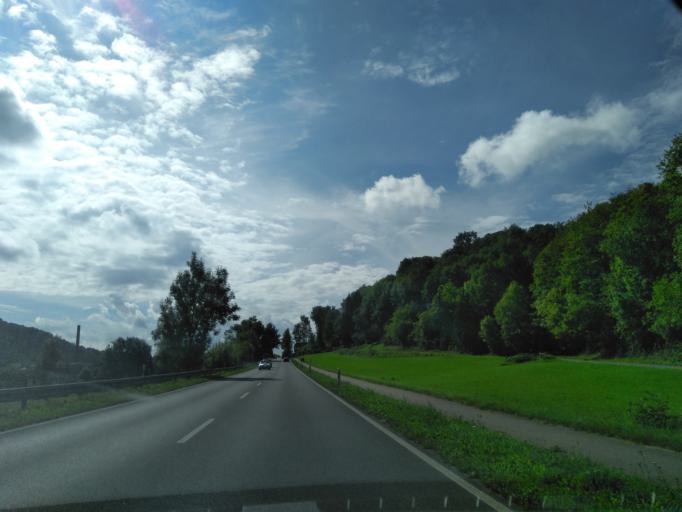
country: DE
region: Baden-Wuerttemberg
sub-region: Regierungsbezirk Stuttgart
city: Besigheim
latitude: 48.9764
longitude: 9.1441
